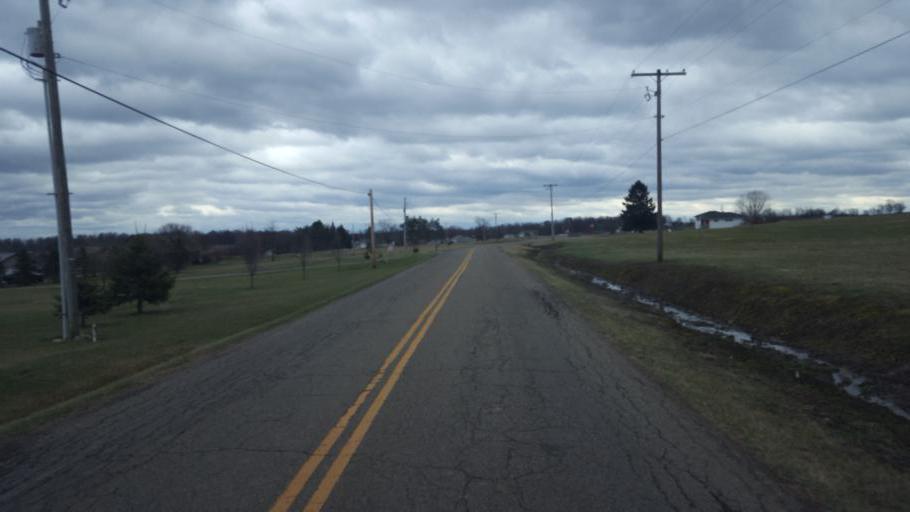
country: US
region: Ohio
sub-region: Licking County
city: Utica
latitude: 40.2433
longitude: -82.4208
